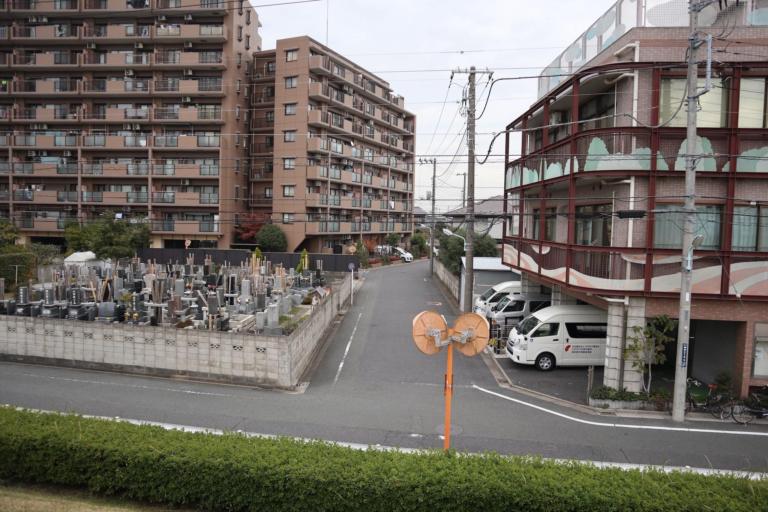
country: JP
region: Chiba
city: Matsudo
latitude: 35.7417
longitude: 139.8663
